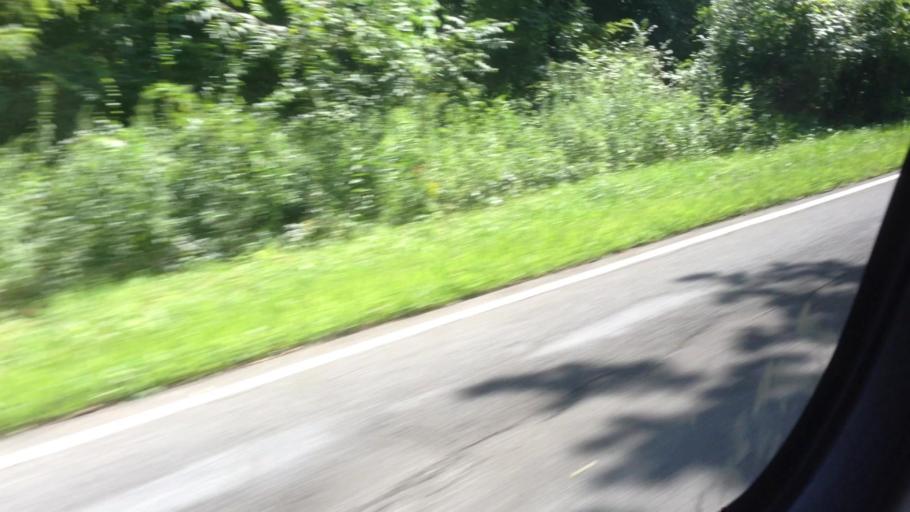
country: US
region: New York
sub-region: Dutchess County
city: Red Hook
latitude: 42.0102
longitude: -73.9099
